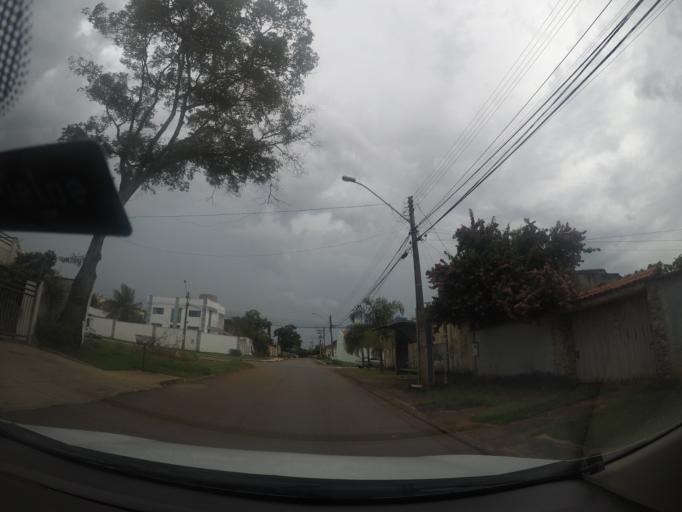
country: BR
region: Goias
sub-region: Goiania
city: Goiania
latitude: -16.6388
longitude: -49.2283
